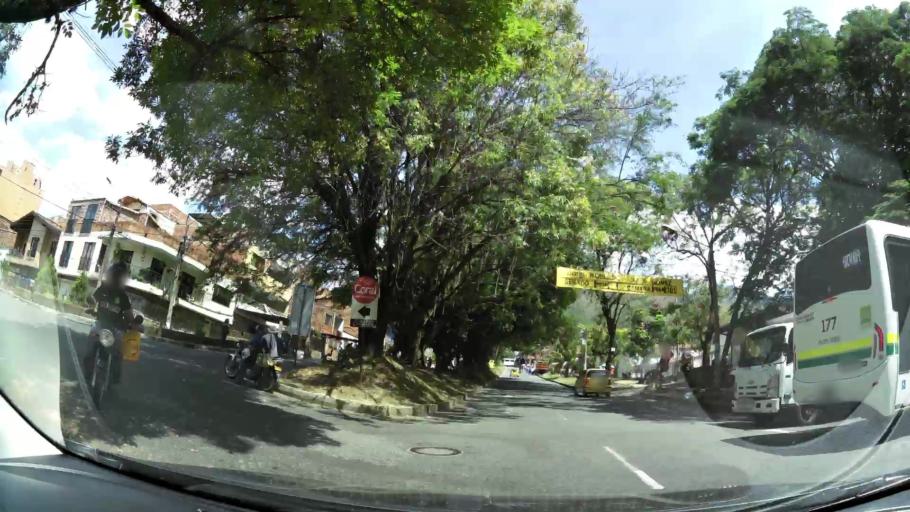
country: CO
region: Antioquia
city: Bello
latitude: 6.3419
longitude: -75.5484
